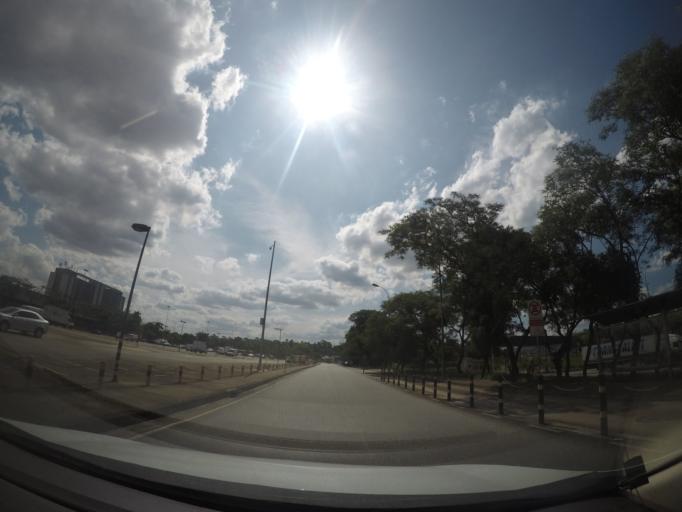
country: BR
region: Sao Paulo
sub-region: Guarulhos
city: Guarulhos
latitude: -23.4240
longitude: -46.4856
